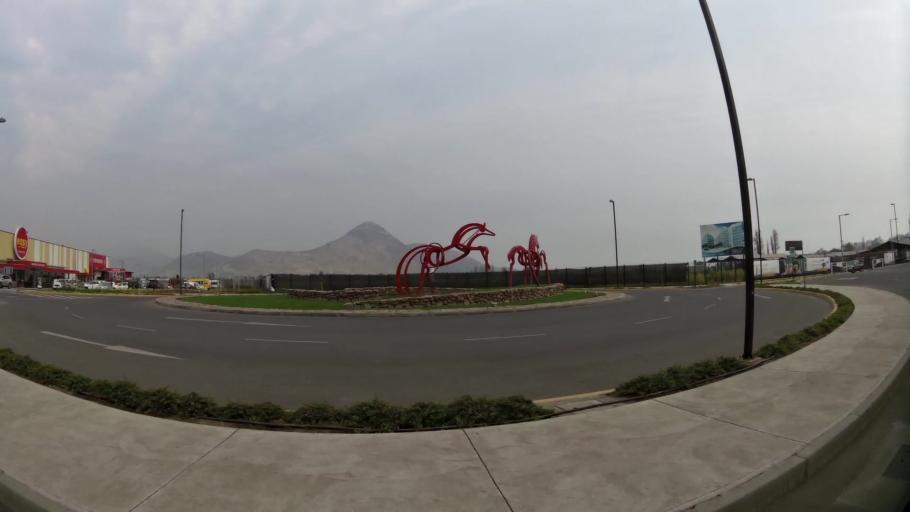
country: CL
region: Santiago Metropolitan
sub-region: Provincia de Chacabuco
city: Chicureo Abajo
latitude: -33.2866
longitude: -70.7000
